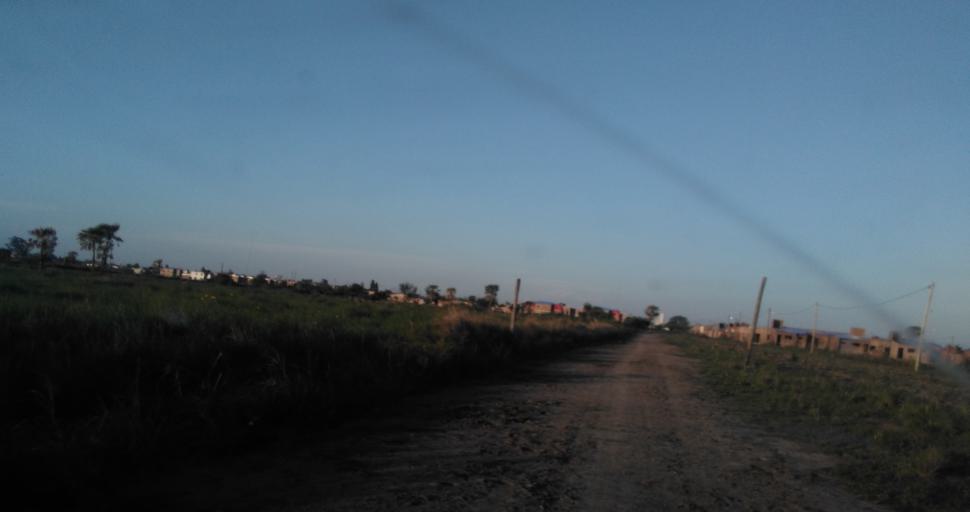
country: AR
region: Chaco
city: Resistencia
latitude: -27.4849
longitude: -59.0155
